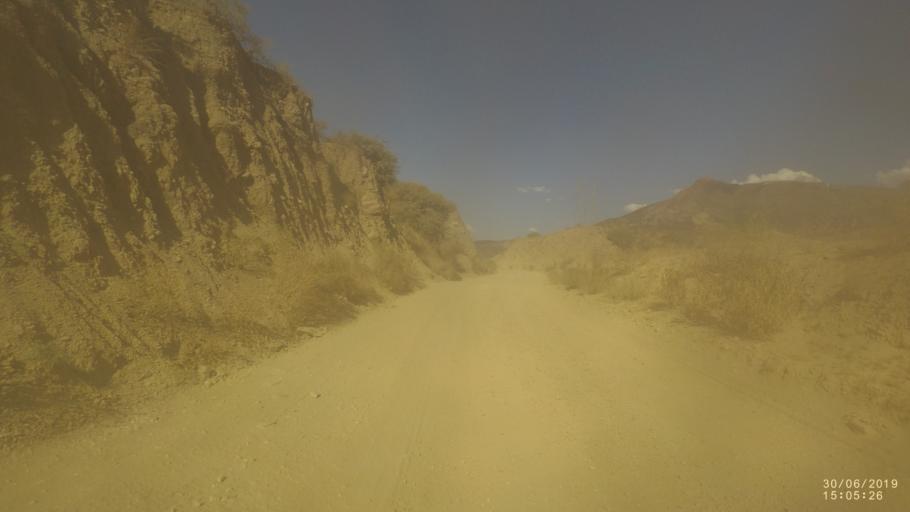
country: BO
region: Cochabamba
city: Irpa Irpa
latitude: -17.7320
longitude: -66.3170
